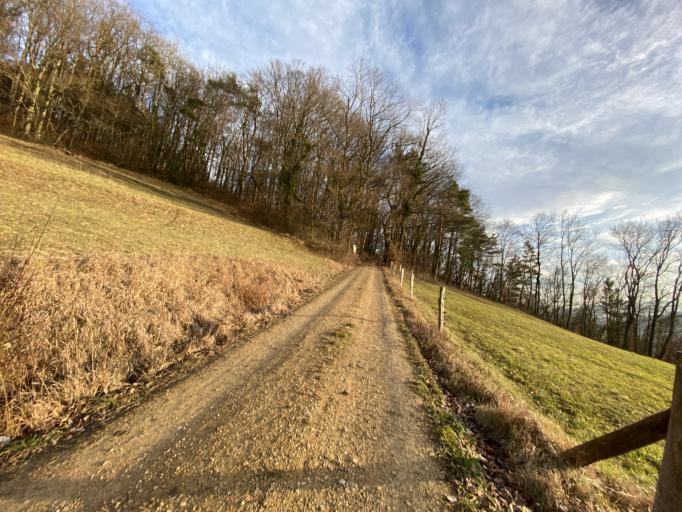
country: CH
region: Aargau
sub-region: Bezirk Laufenburg
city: Frick
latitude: 47.5117
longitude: 8.0366
